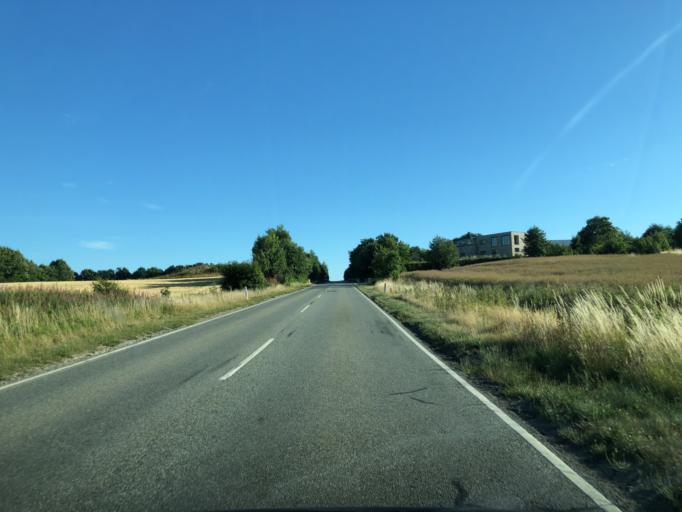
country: DK
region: Central Jutland
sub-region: Arhus Kommune
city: Framlev
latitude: 56.1207
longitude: 9.9896
